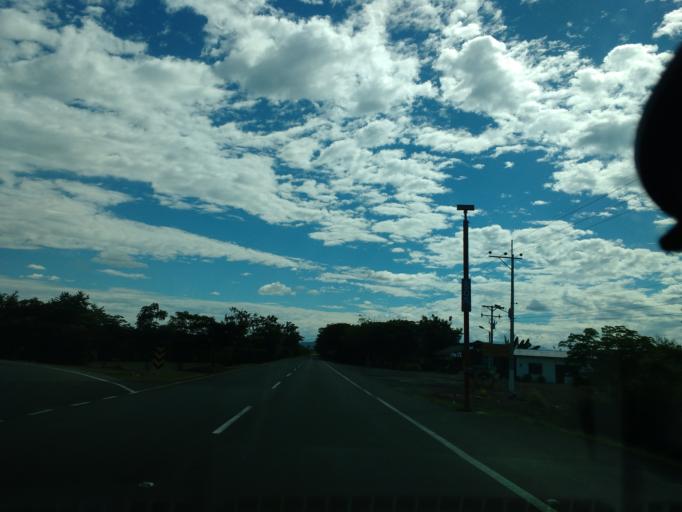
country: CO
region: Tolima
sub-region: Flandes
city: Flandes
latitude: 4.2560
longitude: -74.8374
